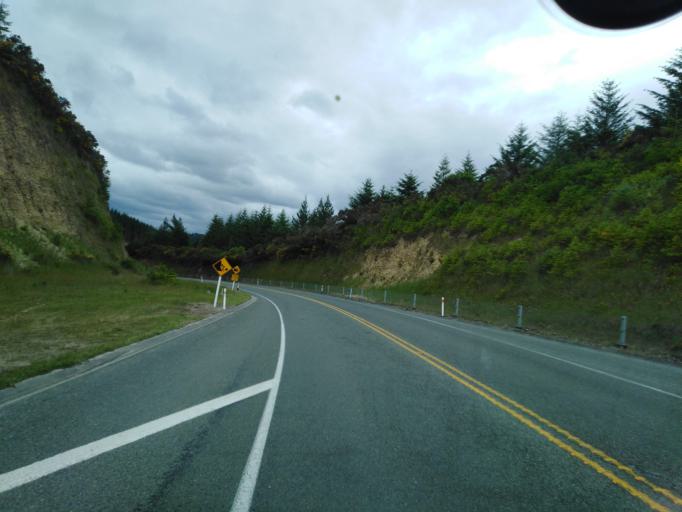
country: NZ
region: Tasman
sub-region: Tasman District
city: Wakefield
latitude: -41.4803
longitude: 172.9074
